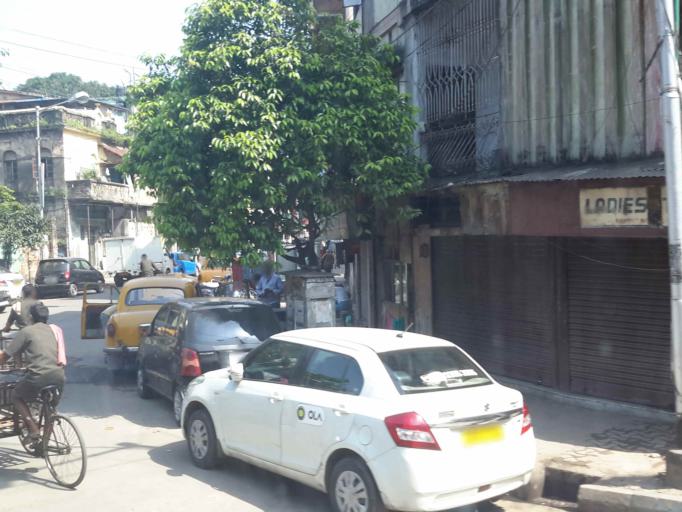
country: IN
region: West Bengal
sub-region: Kolkata
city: Kolkata
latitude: 22.5414
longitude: 88.3649
